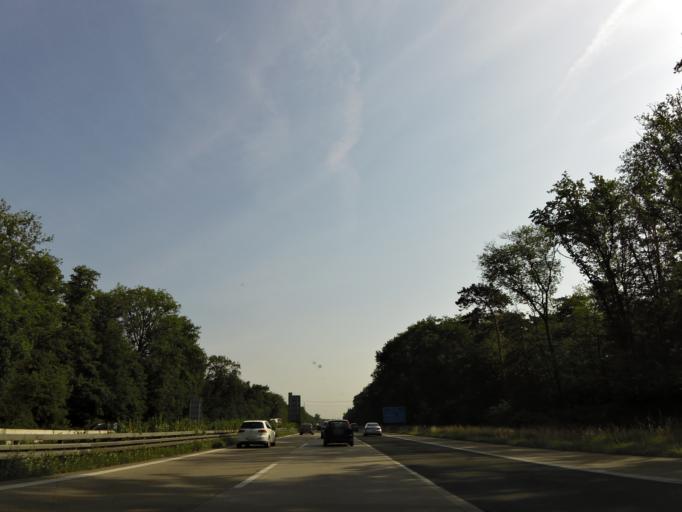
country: DE
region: Baden-Wuerttemberg
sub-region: Karlsruhe Region
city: Forst
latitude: 49.1695
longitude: 8.5733
